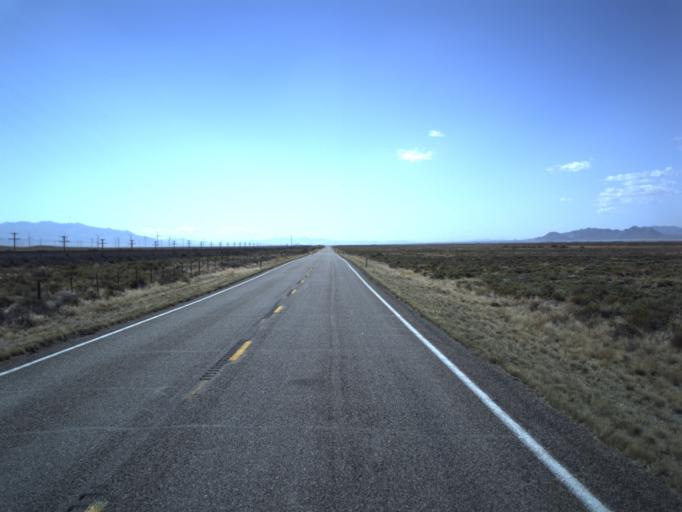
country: US
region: Utah
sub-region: Beaver County
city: Milford
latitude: 38.6443
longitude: -112.9830
